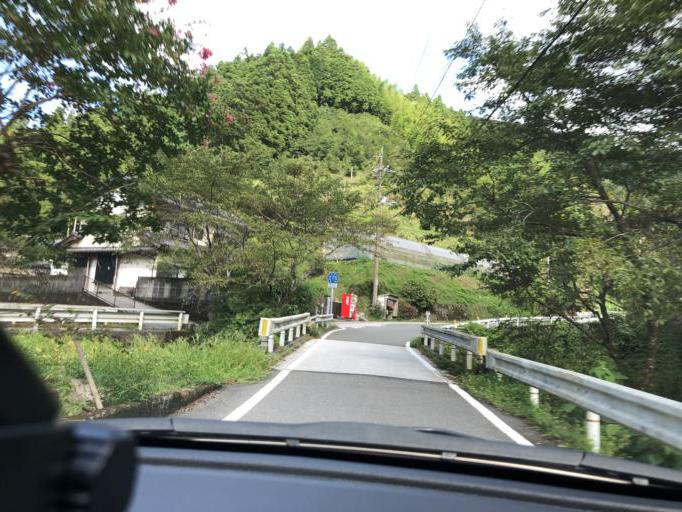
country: JP
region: Kochi
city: Kochi-shi
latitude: 33.6107
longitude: 133.5107
